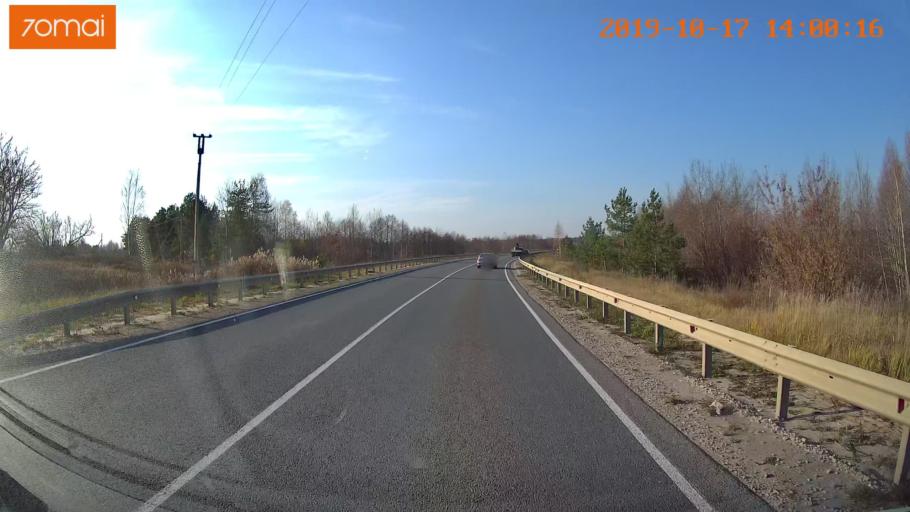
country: RU
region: Rjazan
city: Spas-Klepiki
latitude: 55.1447
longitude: 40.1834
